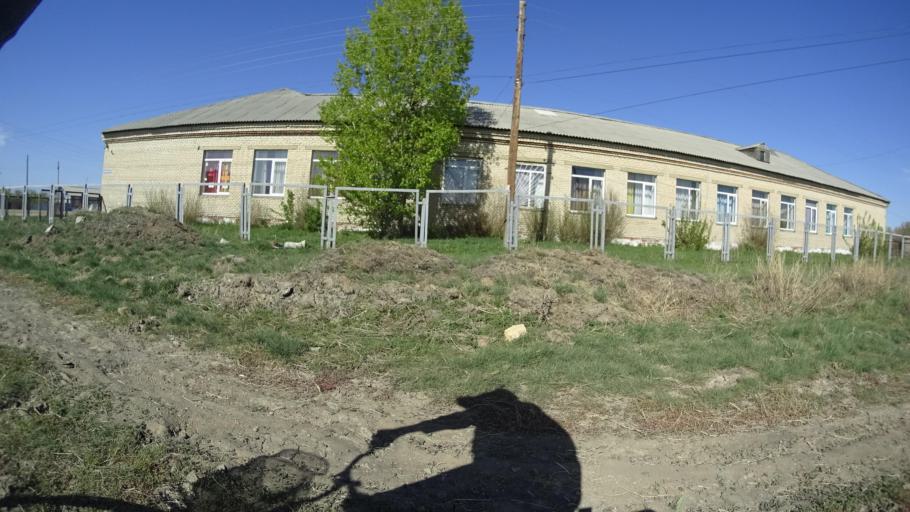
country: RU
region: Chelyabinsk
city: Chesma
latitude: 53.7969
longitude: 61.0327
